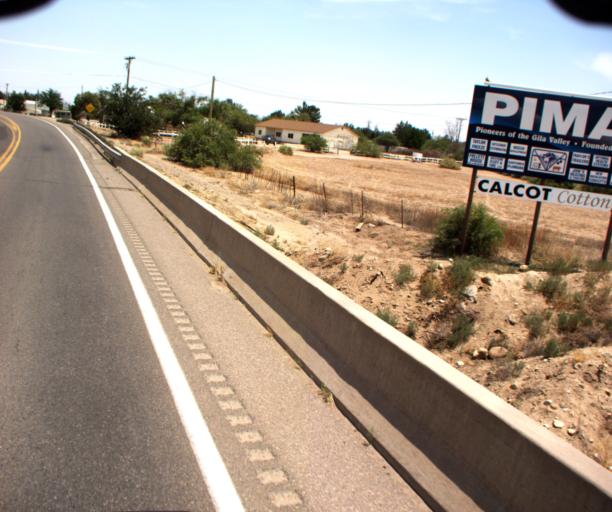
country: US
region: Arizona
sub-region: Graham County
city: Pima
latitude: 32.8969
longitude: -109.8360
